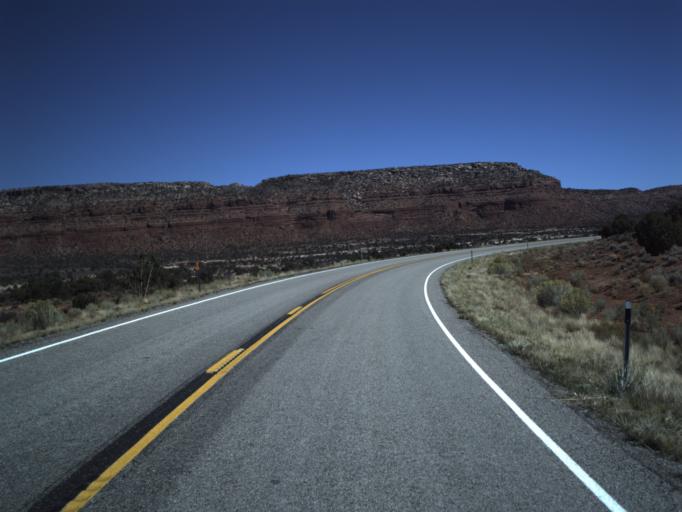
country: US
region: Utah
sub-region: San Juan County
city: Blanding
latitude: 37.6525
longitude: -110.1414
